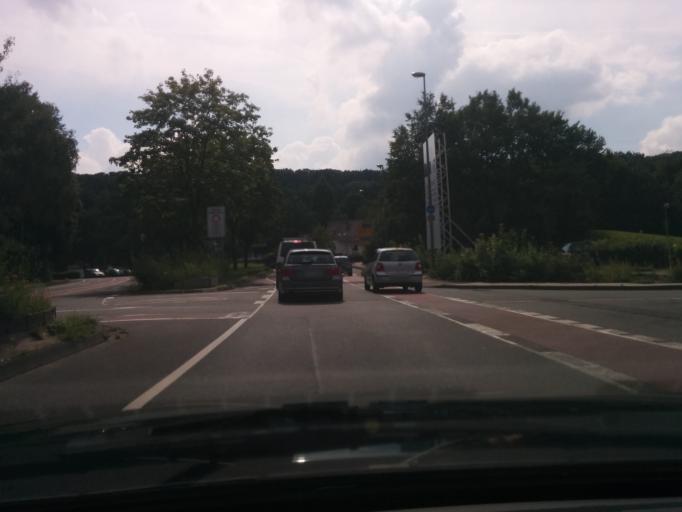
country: DE
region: North Rhine-Westphalia
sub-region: Regierungsbezirk Detmold
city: Bielefeld
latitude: 52.0337
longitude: 8.5001
